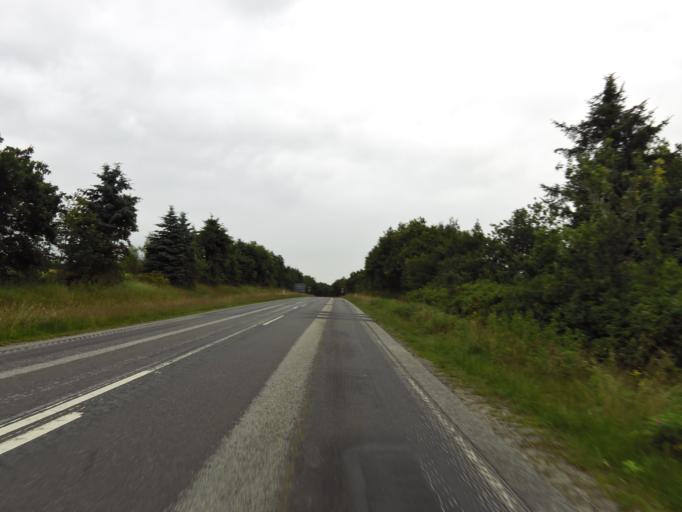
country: DK
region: South Denmark
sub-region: Tonder Kommune
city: Toftlund
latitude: 55.1692
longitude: 8.9649
